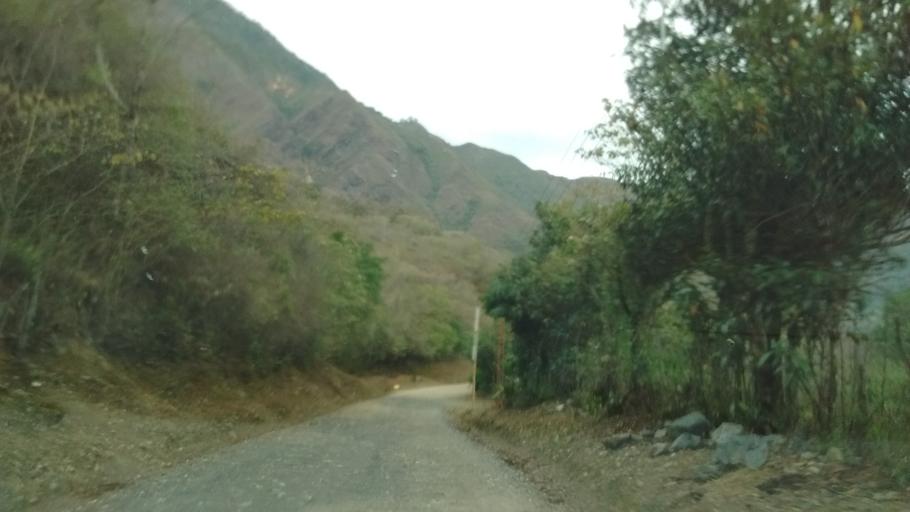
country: CO
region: Cauca
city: Almaguer
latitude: 1.8455
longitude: -76.9045
